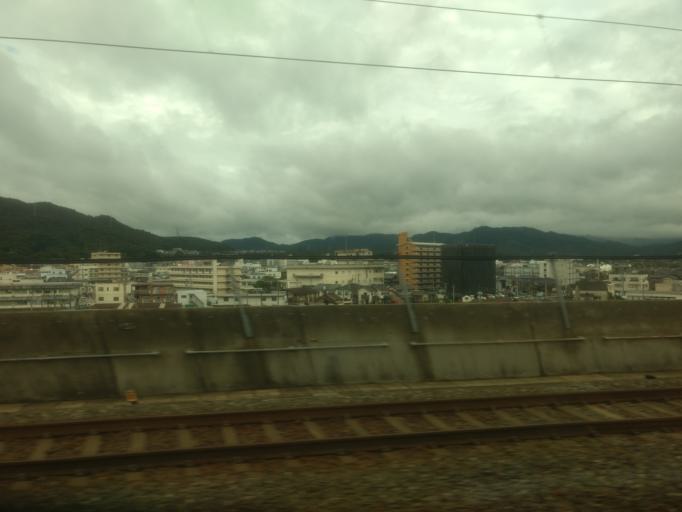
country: JP
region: Yamaguchi
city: Ogori-shimogo
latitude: 34.0949
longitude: 131.4004
